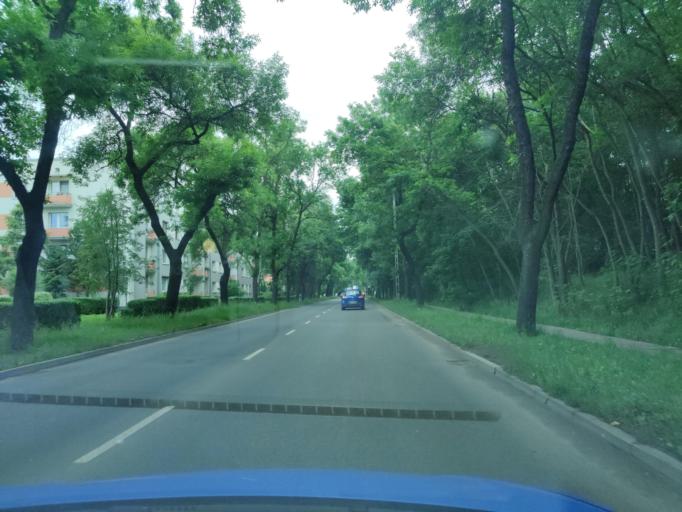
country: PL
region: Silesian Voivodeship
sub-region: Sosnowiec
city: Sosnowiec
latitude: 50.2702
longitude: 19.1470
